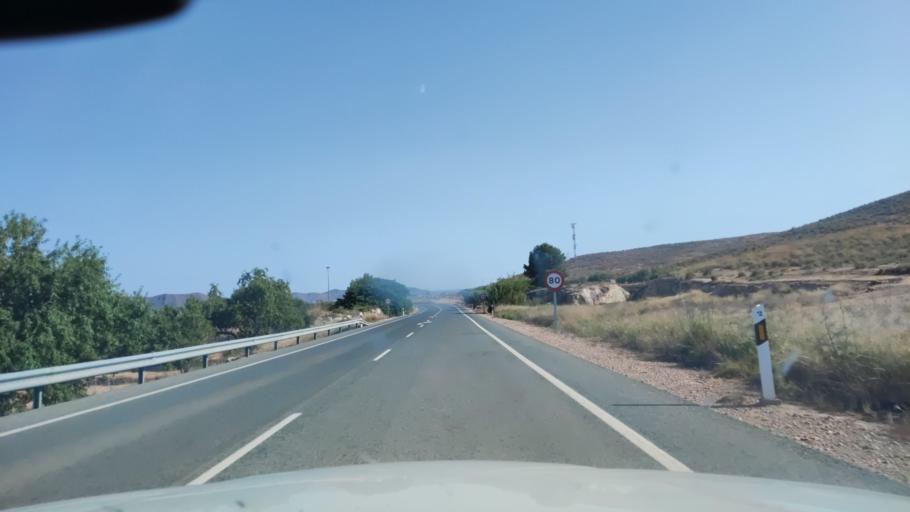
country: ES
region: Castille-La Mancha
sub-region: Provincia de Albacete
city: Tobarra
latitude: 38.6088
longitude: -1.6824
